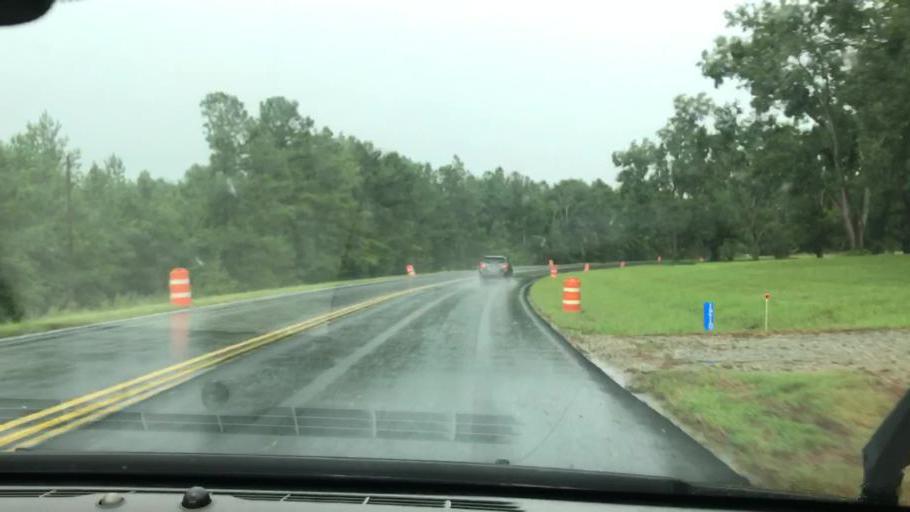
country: US
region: Georgia
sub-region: Clay County
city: Fort Gaines
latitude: 31.5709
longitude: -85.0176
